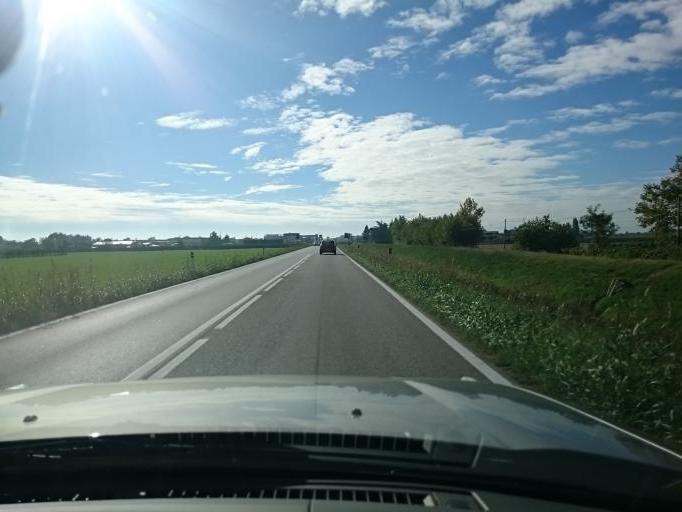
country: IT
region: Veneto
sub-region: Provincia di Padova
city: Bovolenta
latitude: 45.2841
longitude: 11.9281
